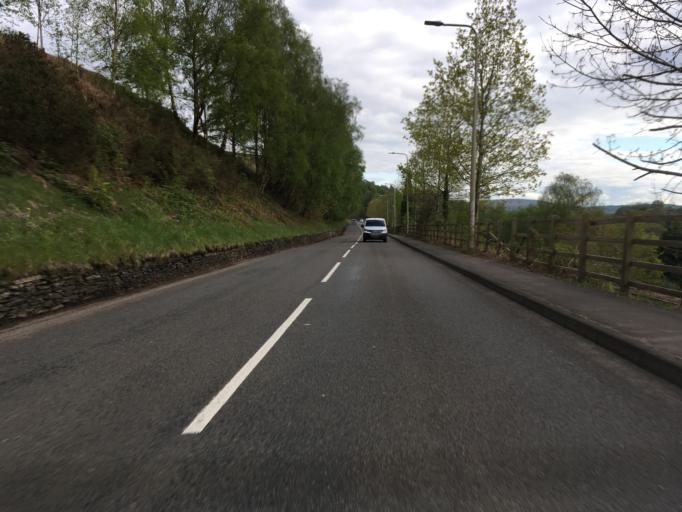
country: GB
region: Wales
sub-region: Merthyr Tydfil County Borough
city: Treharris
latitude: 51.6829
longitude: -3.2963
